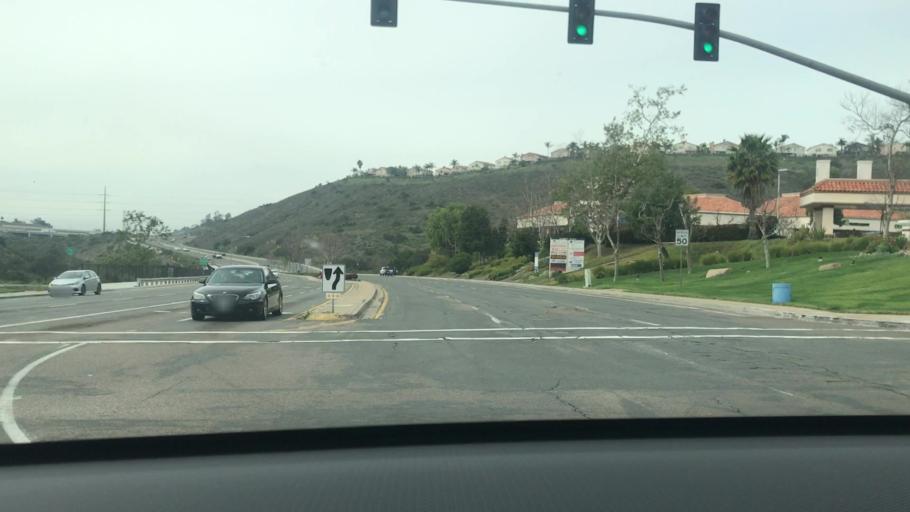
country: US
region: California
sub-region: San Diego County
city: Poway
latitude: 32.9470
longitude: -117.0959
